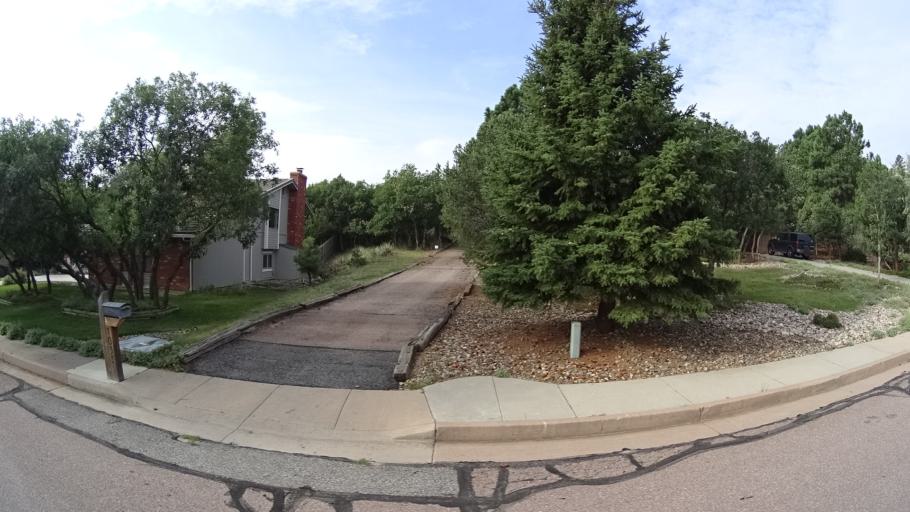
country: US
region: Colorado
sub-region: El Paso County
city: Air Force Academy
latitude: 38.9325
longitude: -104.8473
